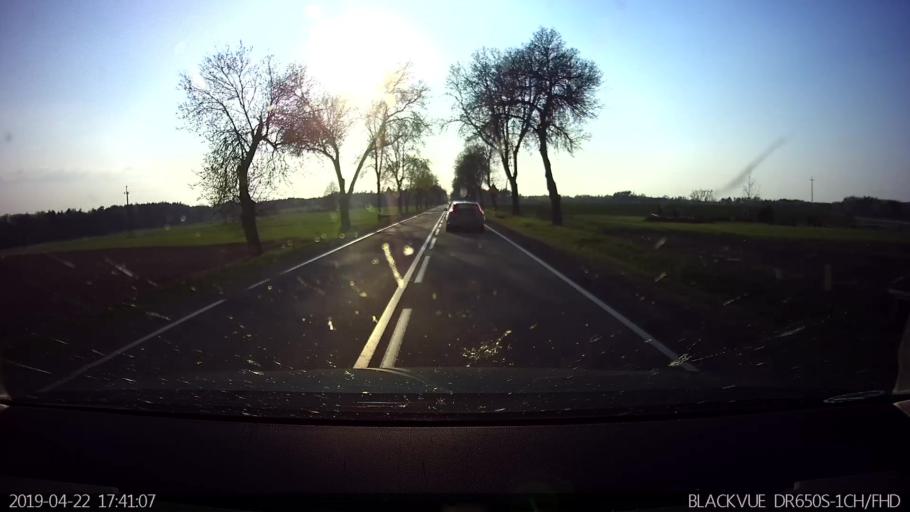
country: PL
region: Masovian Voivodeship
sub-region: Powiat wegrowski
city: Miedzna
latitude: 52.4015
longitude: 22.1149
